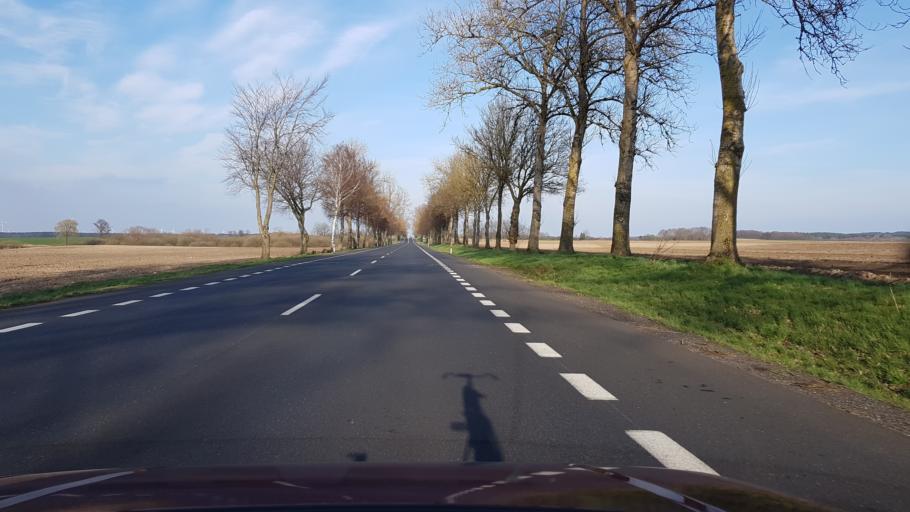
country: PL
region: West Pomeranian Voivodeship
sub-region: Powiat kolobrzeski
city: Goscino
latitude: 53.9865
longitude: 15.7186
